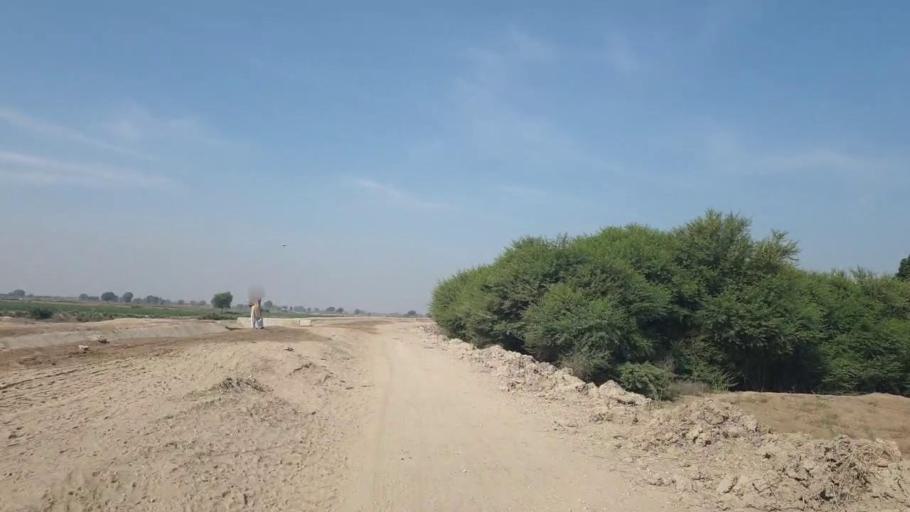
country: PK
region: Sindh
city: Matiari
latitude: 25.6834
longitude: 68.3362
